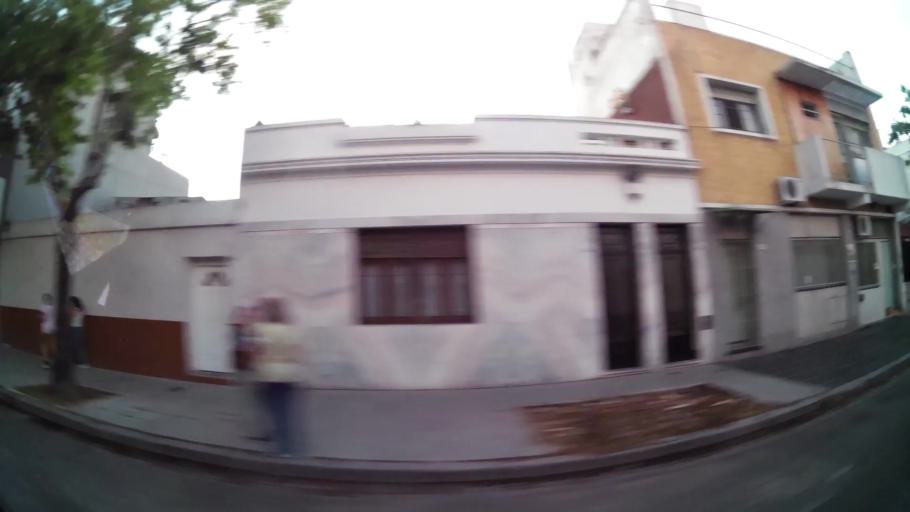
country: AR
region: Buenos Aires F.D.
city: Villa Santa Rita
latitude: -34.6361
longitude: -58.4369
